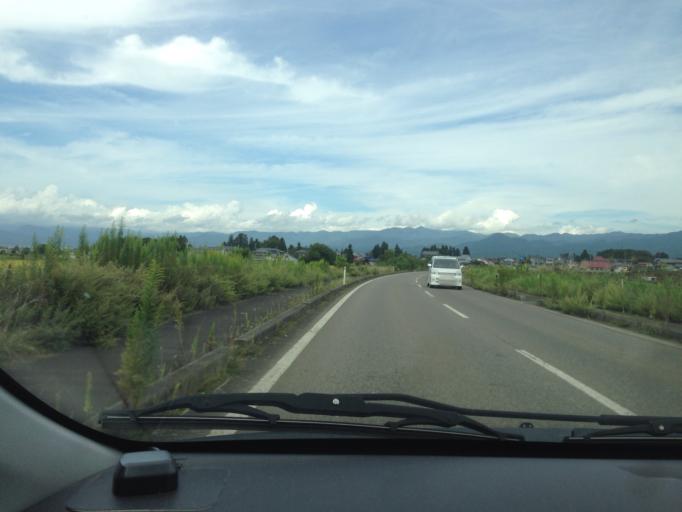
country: JP
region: Fukushima
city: Kitakata
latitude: 37.6062
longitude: 139.9112
